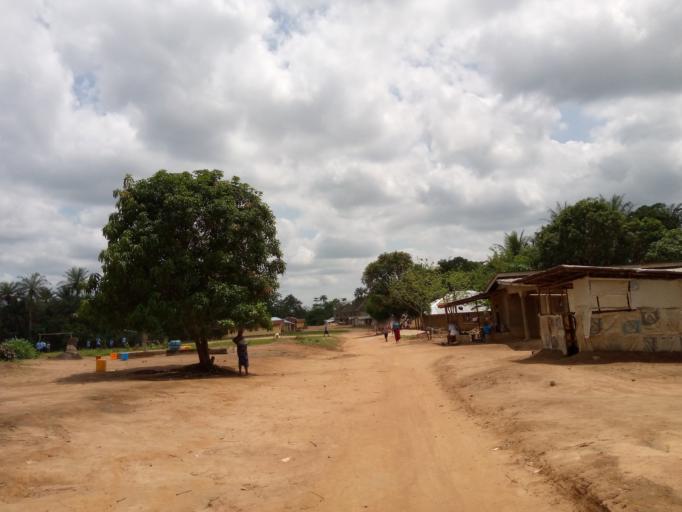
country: SL
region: Western Area
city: Waterloo
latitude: 8.4023
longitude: -12.9492
